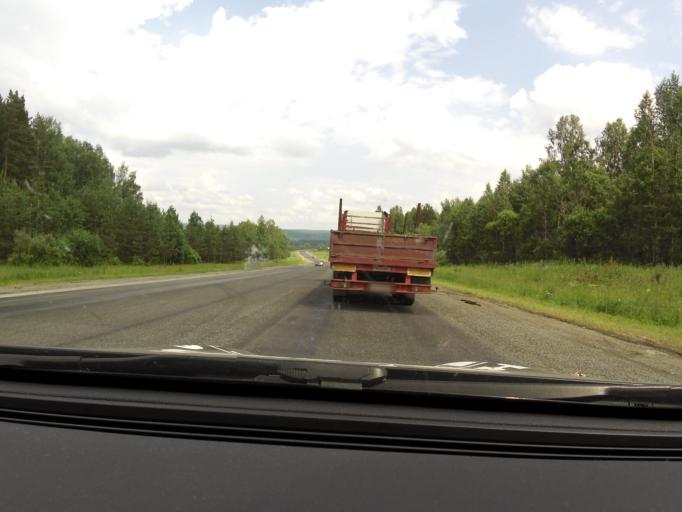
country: RU
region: Sverdlovsk
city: Ufimskiy
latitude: 56.7874
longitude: 58.3242
